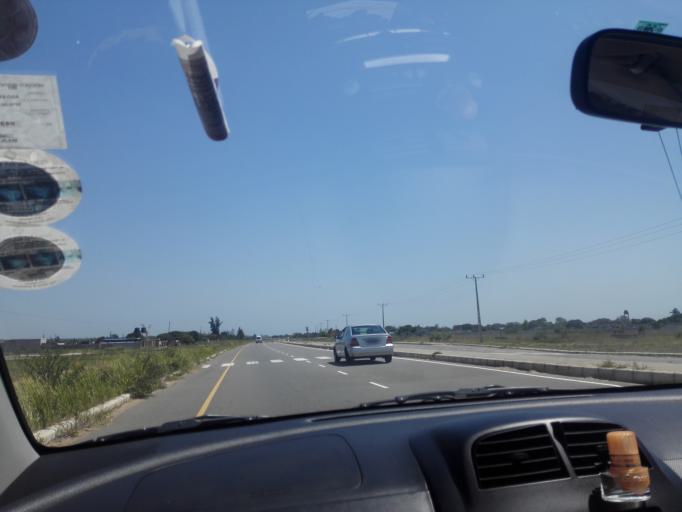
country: MZ
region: Maputo City
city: Maputo
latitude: -25.8084
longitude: 32.6722
